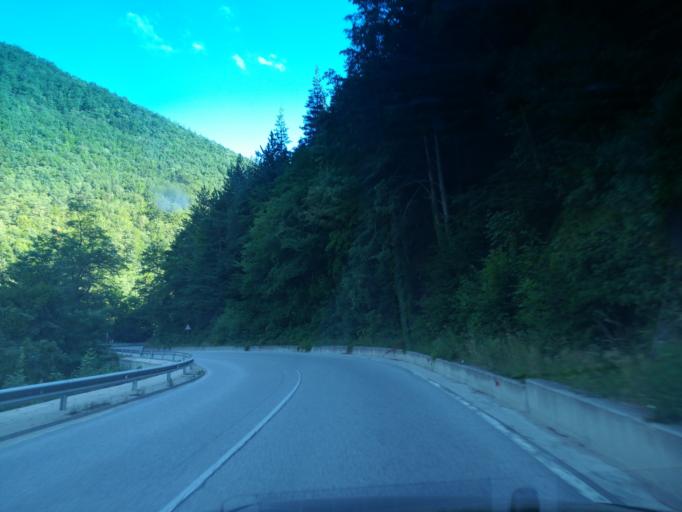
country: BG
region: Smolyan
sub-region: Obshtina Chepelare
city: Chepelare
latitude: 41.7949
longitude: 24.7105
